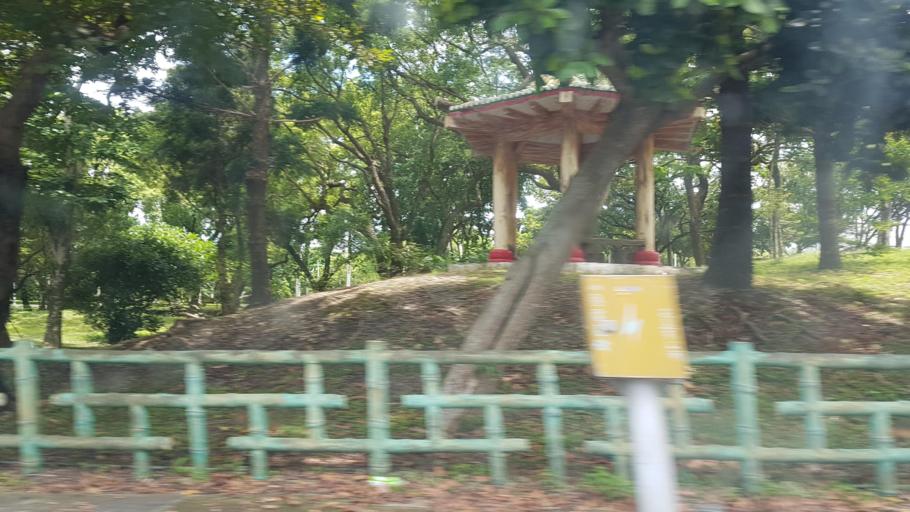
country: TW
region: Taiwan
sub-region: Hualien
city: Hualian
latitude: 23.9901
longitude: 121.6202
